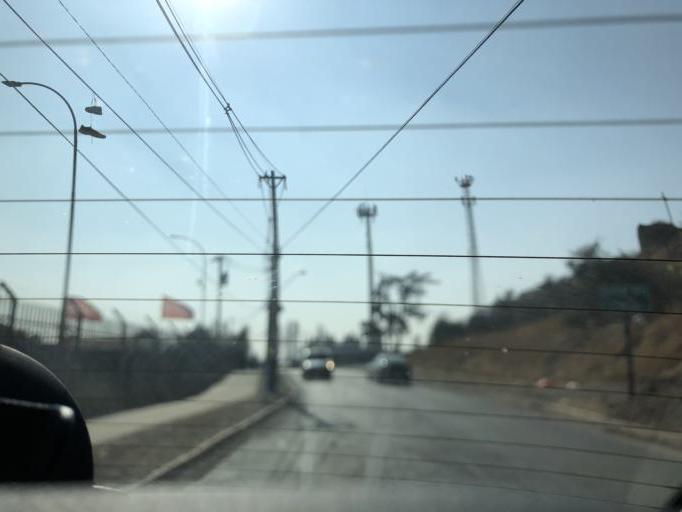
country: CL
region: Santiago Metropolitan
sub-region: Provincia de Cordillera
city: Puente Alto
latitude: -33.6177
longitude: -70.6033
